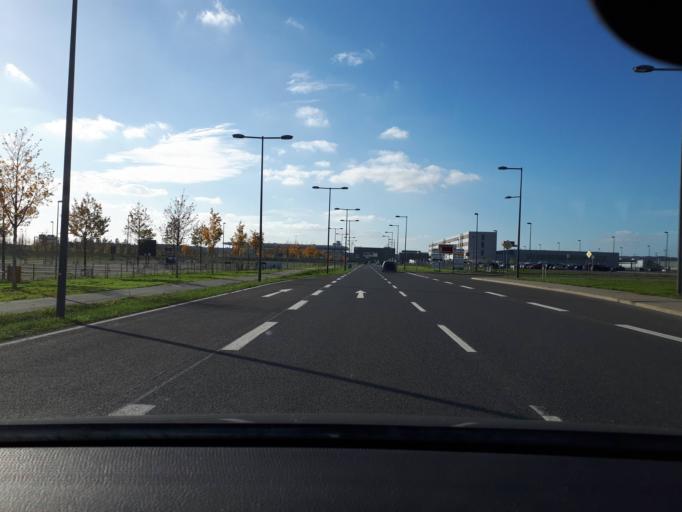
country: DE
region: Brandenburg
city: Schonefeld
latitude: 52.3692
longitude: 13.5237
